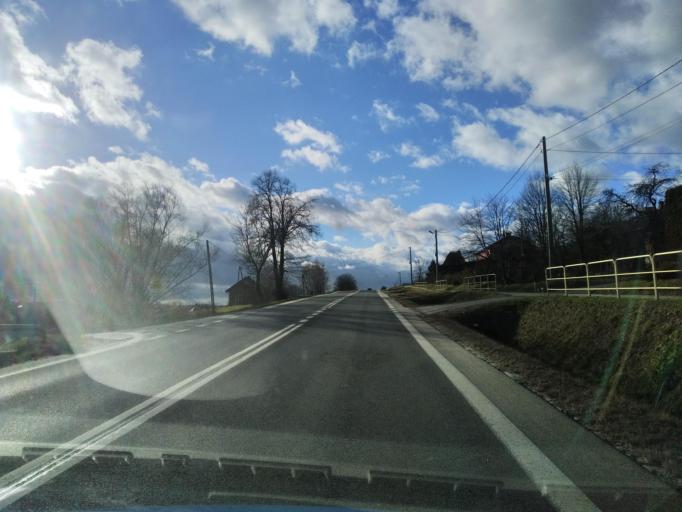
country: PL
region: Lesser Poland Voivodeship
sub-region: Powiat gorlicki
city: Biecz
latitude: 49.7546
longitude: 21.2952
